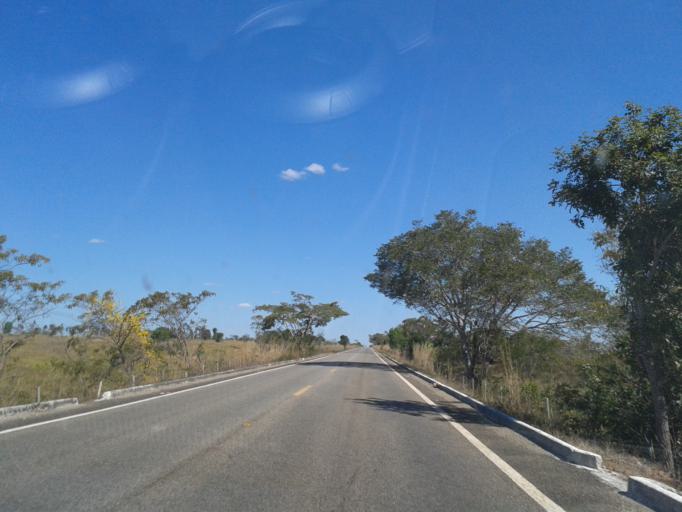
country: BR
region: Goias
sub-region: Sao Miguel Do Araguaia
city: Sao Miguel do Araguaia
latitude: -13.6360
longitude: -50.3139
